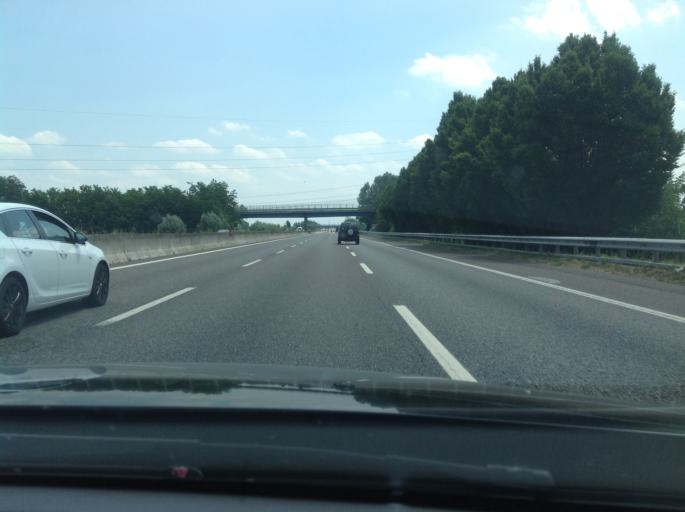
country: IT
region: Lombardy
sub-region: Provincia di Lodi
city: San Rocco al Porto
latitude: 45.0977
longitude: 9.7010
